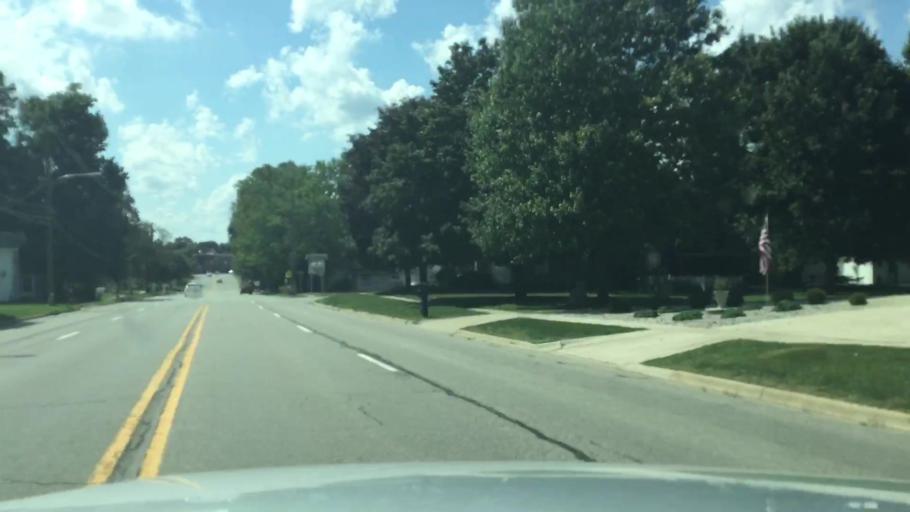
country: US
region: Michigan
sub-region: Lenawee County
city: Clinton
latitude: 42.0744
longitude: -83.9669
